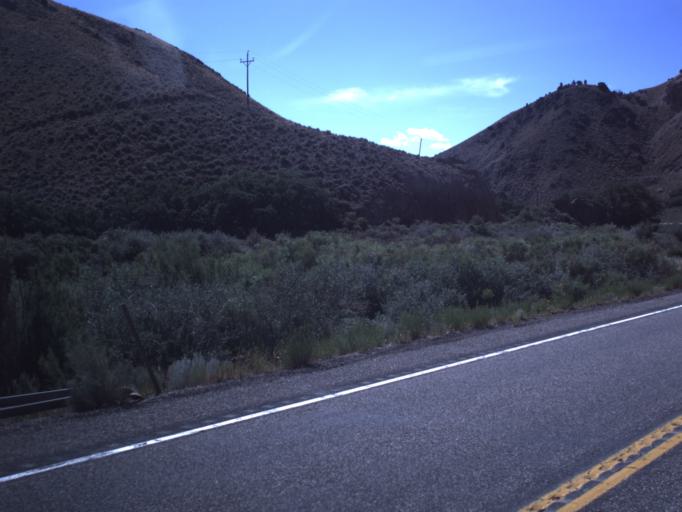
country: US
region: Utah
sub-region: Sevier County
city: Monroe
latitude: 38.4995
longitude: -112.2573
